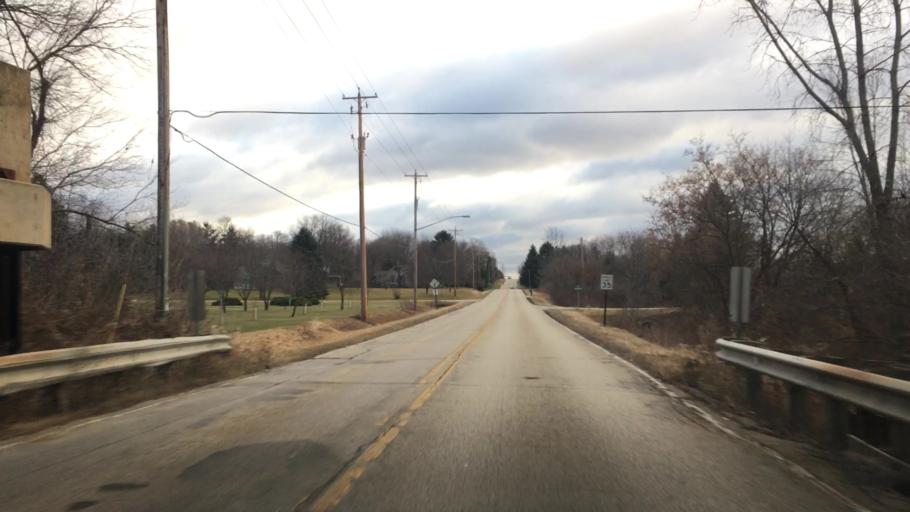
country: US
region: Wisconsin
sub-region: Washington County
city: Richfield
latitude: 43.2364
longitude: -88.2172
